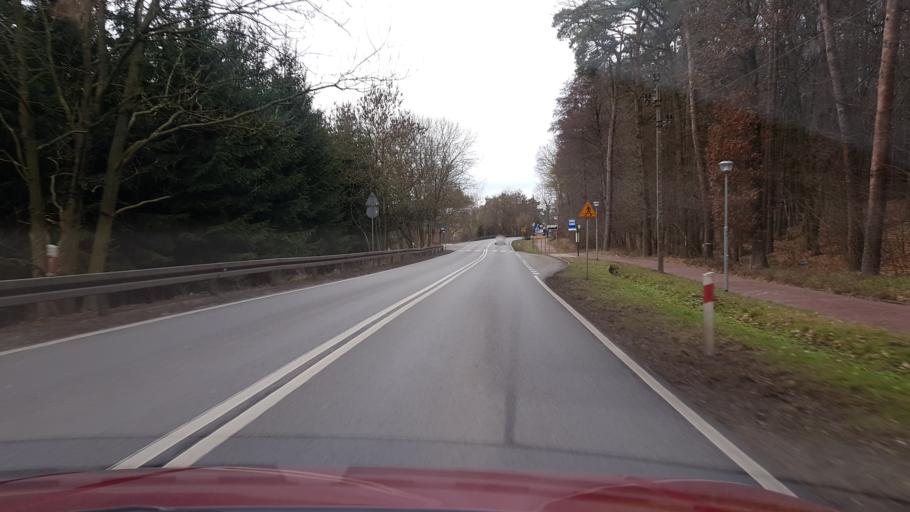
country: PL
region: West Pomeranian Voivodeship
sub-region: Szczecin
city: Szczecin
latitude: 53.4884
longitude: 14.4822
